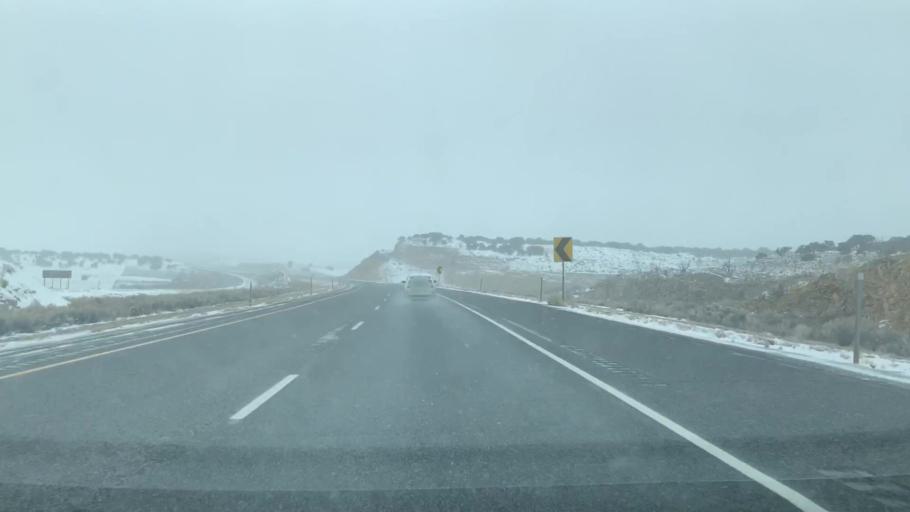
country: US
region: Utah
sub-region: Emery County
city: Castle Dale
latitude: 38.8908
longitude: -110.6429
